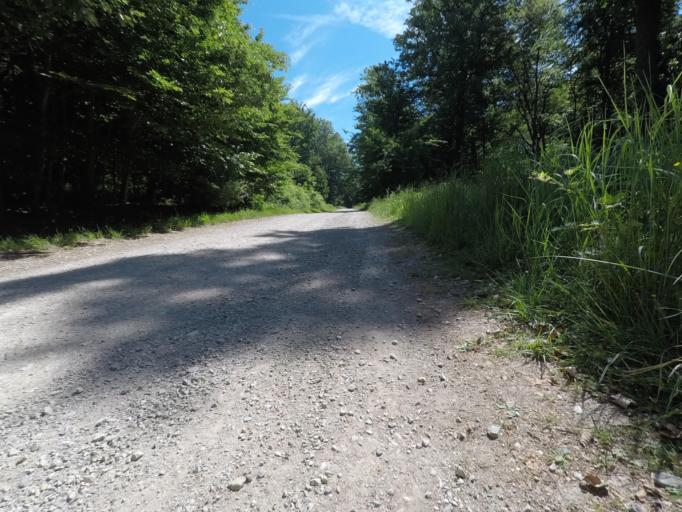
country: AT
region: Lower Austria
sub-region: Politischer Bezirk Modling
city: Laab im Walde
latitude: 48.1791
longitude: 16.2343
